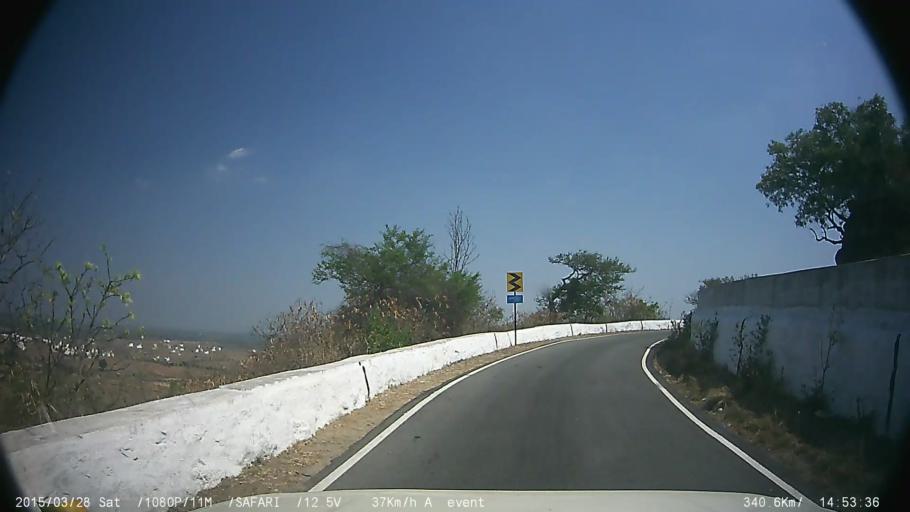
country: IN
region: Karnataka
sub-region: Mysore
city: Mysore
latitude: 12.2857
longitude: 76.6982
